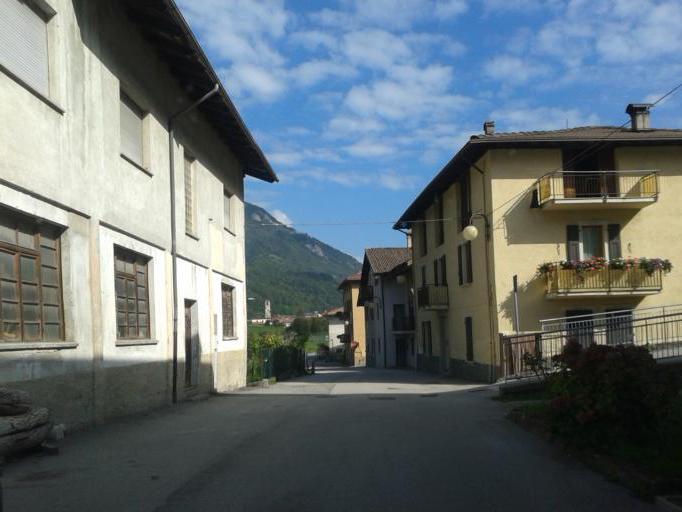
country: IT
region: Trentino-Alto Adige
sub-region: Provincia di Trento
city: Prezzo
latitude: 45.9299
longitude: 10.6369
